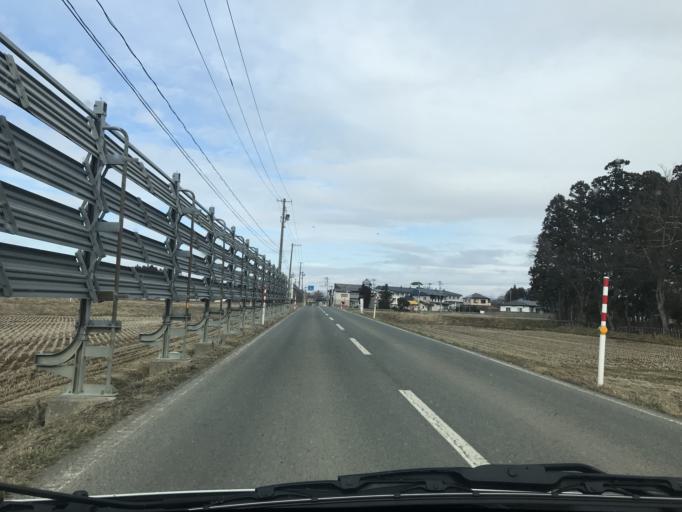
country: JP
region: Iwate
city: Hanamaki
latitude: 39.3444
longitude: 141.0447
